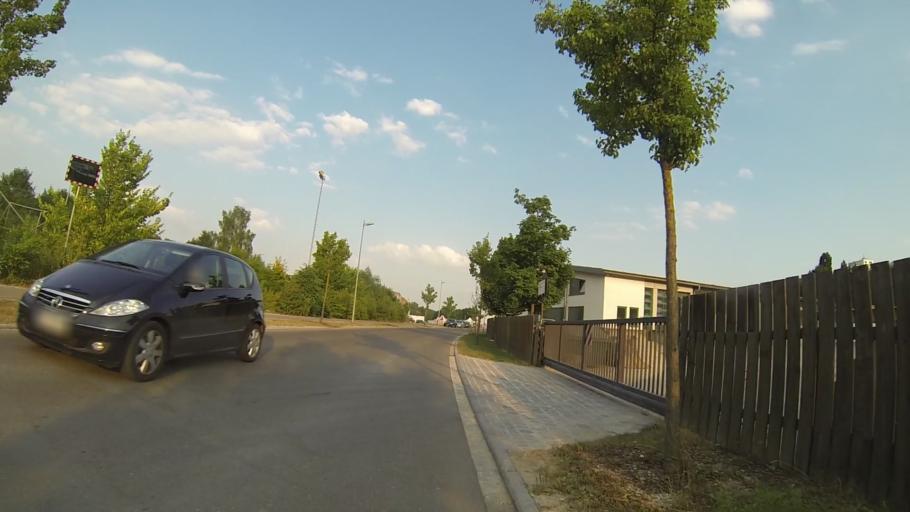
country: DE
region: Baden-Wuerttemberg
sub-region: Tuebingen Region
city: Dornstadt
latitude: 48.4194
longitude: 9.9126
